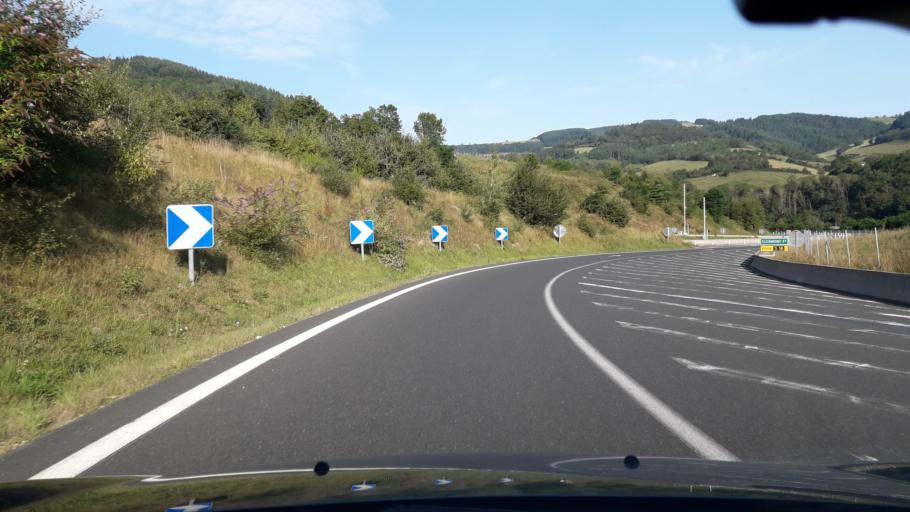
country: FR
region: Rhone-Alpes
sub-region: Departement du Rhone
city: Tarare
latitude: 45.8893
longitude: 4.4092
